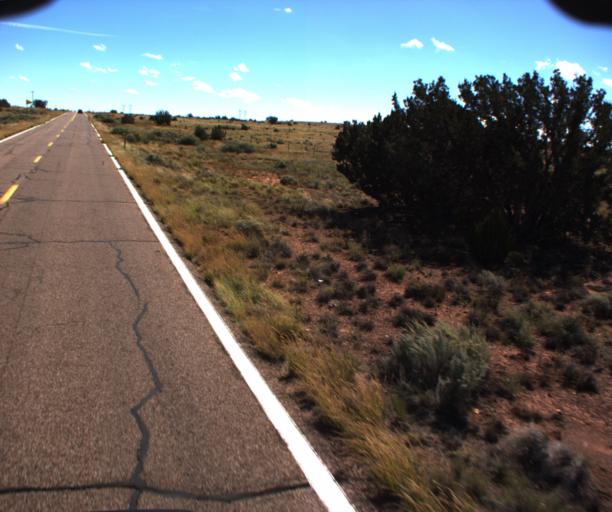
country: US
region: Arizona
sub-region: Apache County
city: Saint Johns
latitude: 34.5726
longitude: -109.6359
